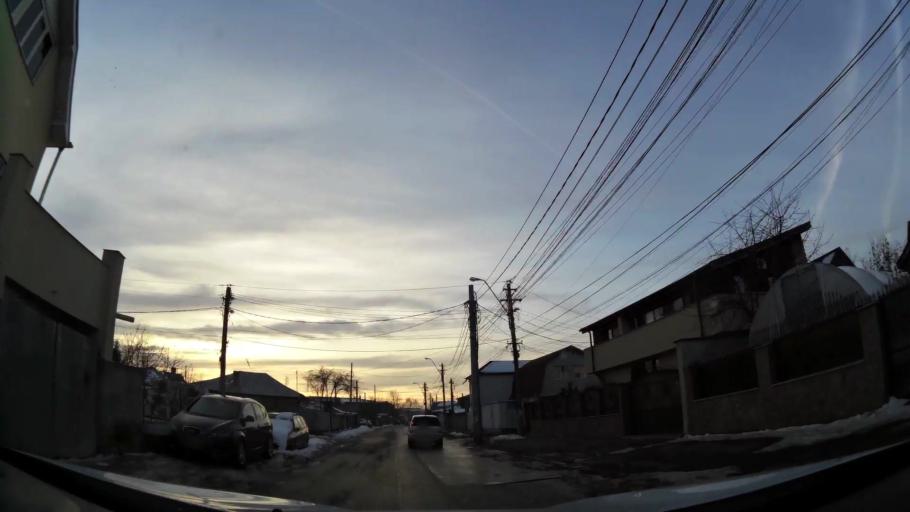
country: RO
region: Ilfov
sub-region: Comuna Magurele
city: Magurele
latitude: 44.3926
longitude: 26.0381
